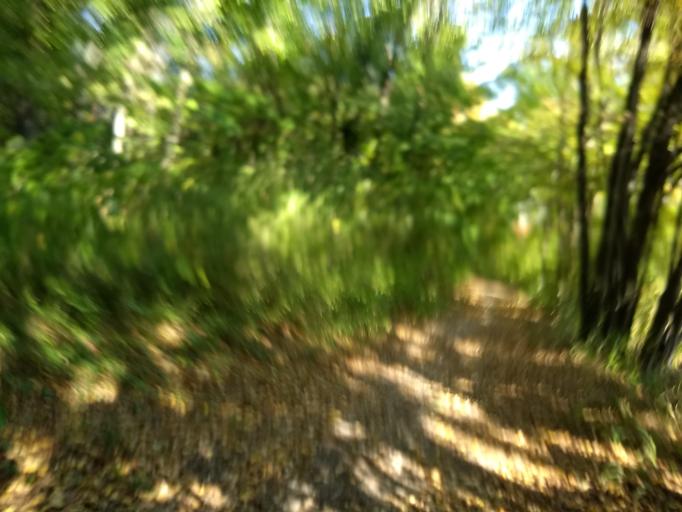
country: AT
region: Lower Austria
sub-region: Politischer Bezirk Modling
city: Giesshubl
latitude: 48.1062
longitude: 16.2401
